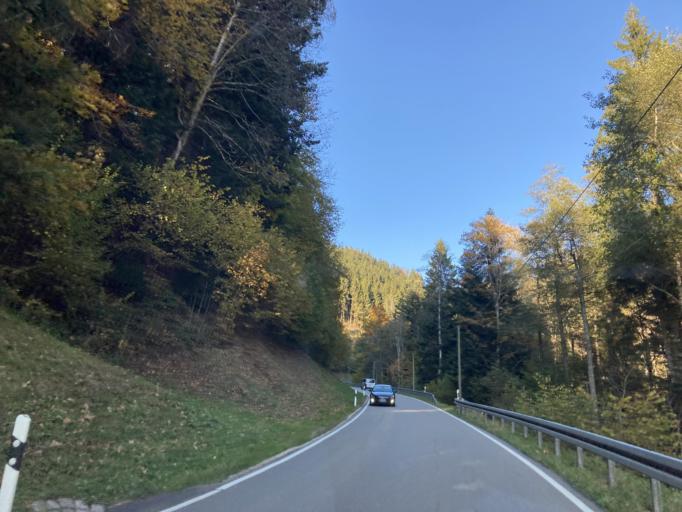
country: DE
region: Baden-Wuerttemberg
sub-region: Freiburg Region
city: Sankt Margen
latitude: 47.9712
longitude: 8.0888
